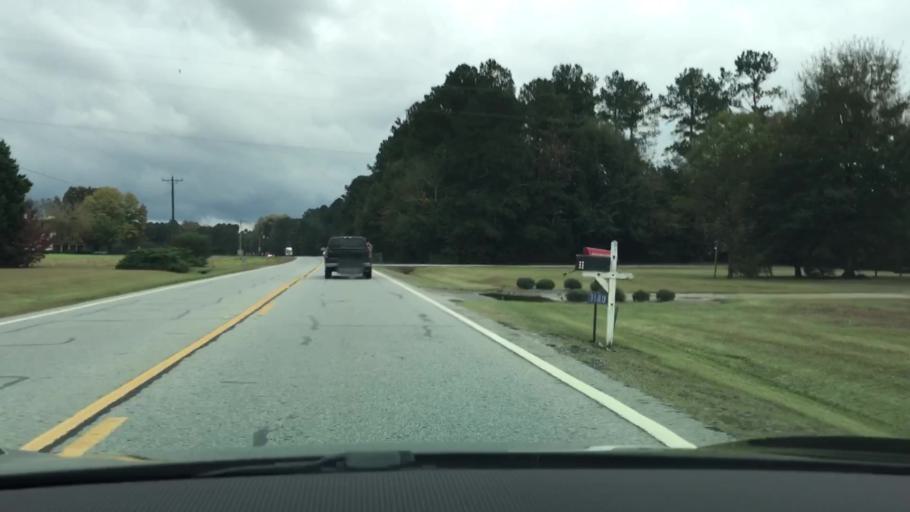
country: US
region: Georgia
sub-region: Oconee County
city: Watkinsville
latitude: 33.8155
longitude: -83.3616
